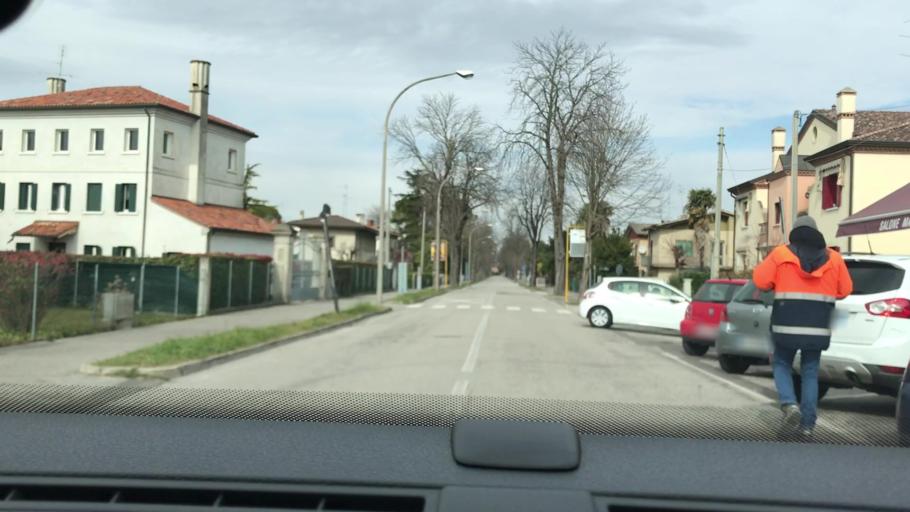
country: IT
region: Veneto
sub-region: Provincia di Venezia
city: Santo Stino di Livenza
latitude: 45.7210
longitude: 12.6815
